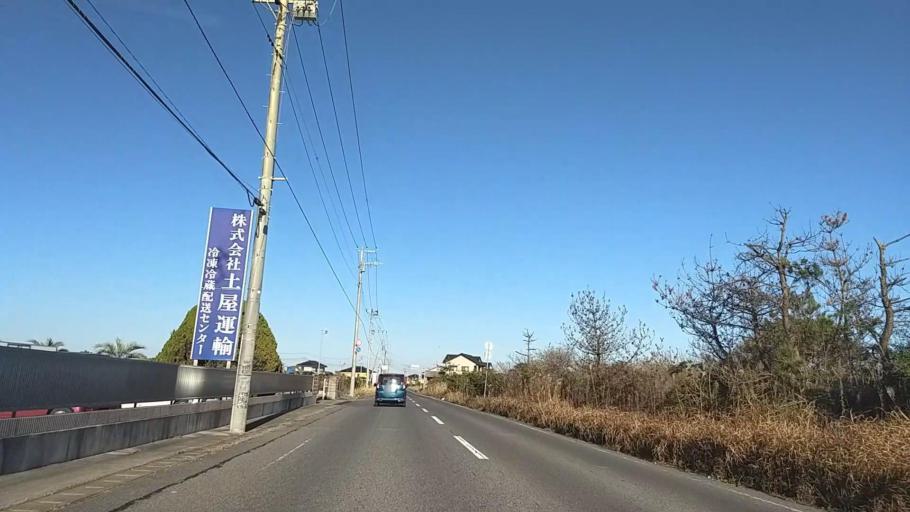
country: JP
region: Chiba
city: Asahi
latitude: 35.6745
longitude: 140.6220
